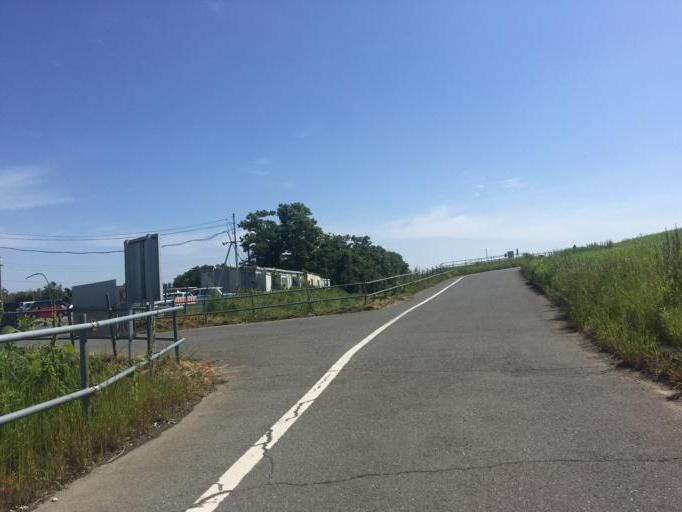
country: JP
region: Saitama
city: Shiki
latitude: 35.8583
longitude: 139.5922
